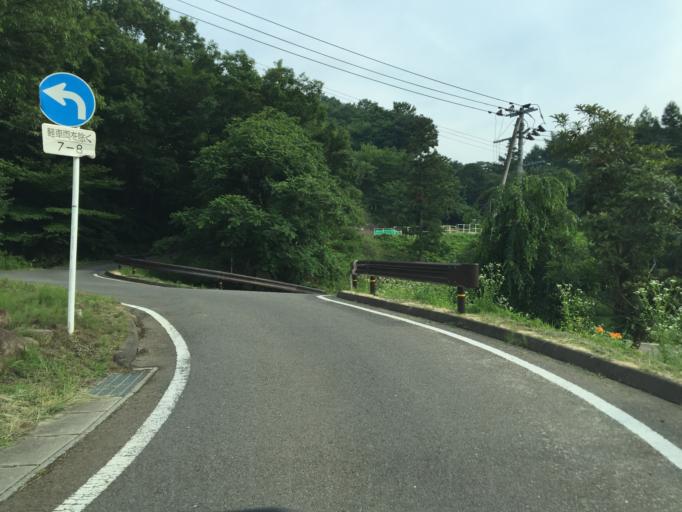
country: JP
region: Fukushima
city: Fukushima-shi
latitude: 37.7307
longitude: 140.4804
